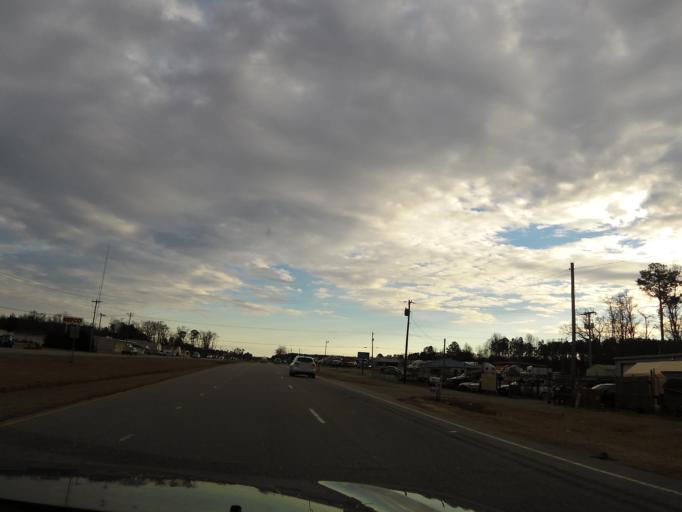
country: US
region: North Carolina
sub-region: Nash County
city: Sharpsburg
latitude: 35.9042
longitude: -77.8275
